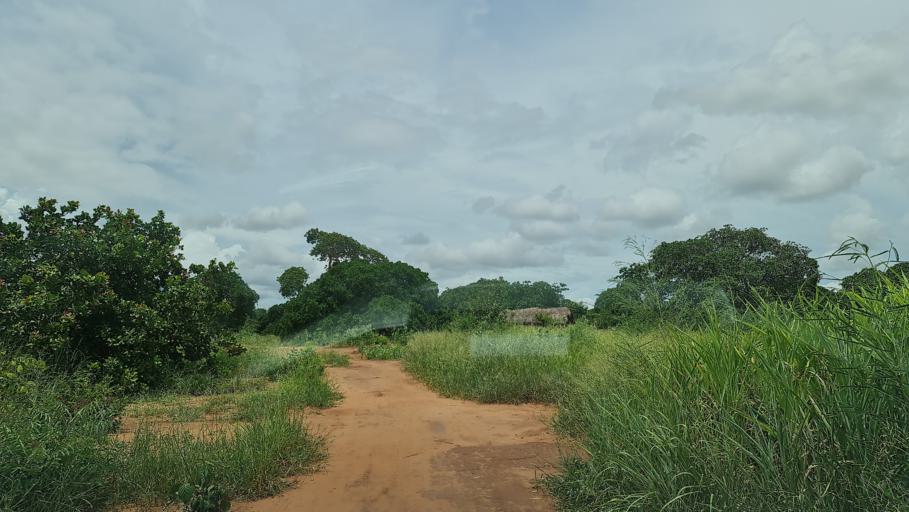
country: MZ
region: Nampula
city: Nacala
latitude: -14.7913
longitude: 39.9661
